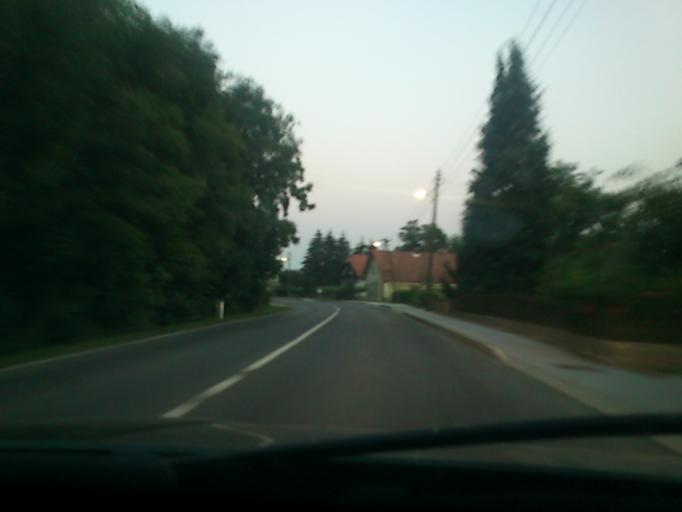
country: SI
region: Duplek
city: Spodnji Duplek
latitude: 46.4861
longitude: 15.7317
